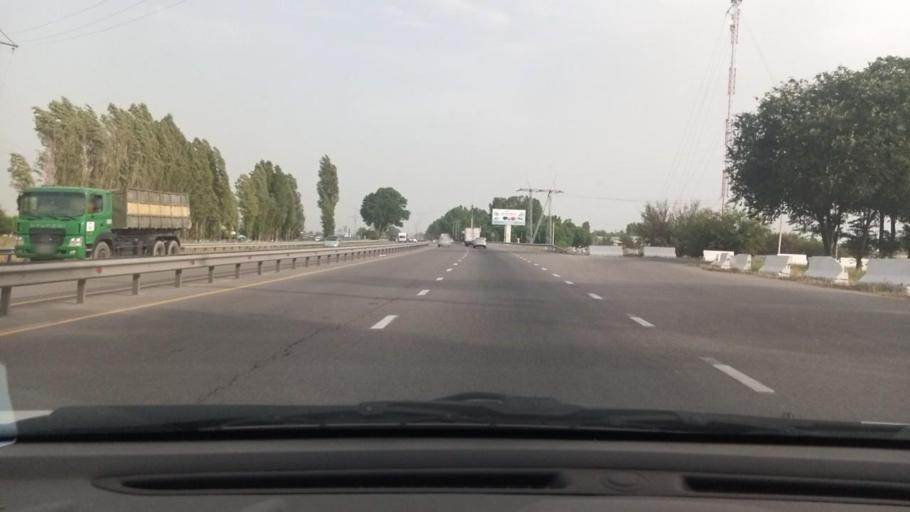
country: UZ
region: Toshkent Shahri
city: Bektemir
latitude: 41.1854
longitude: 69.4041
